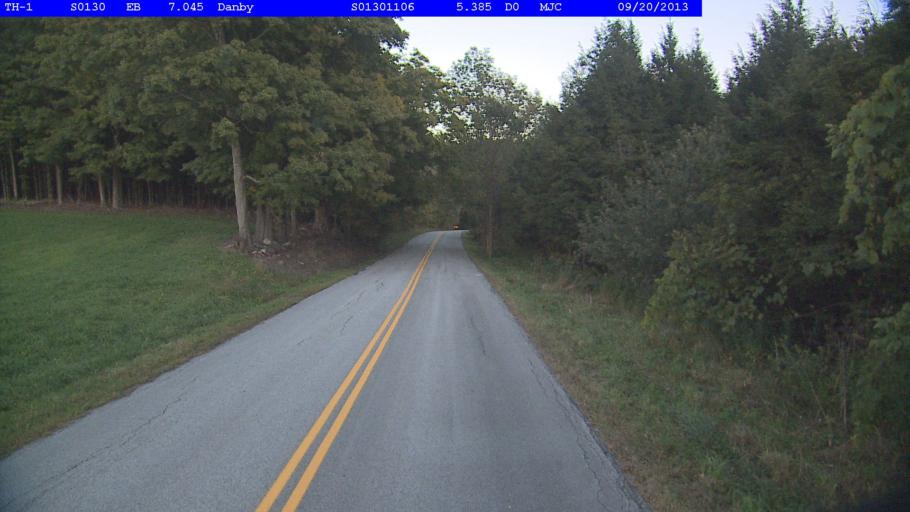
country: US
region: Vermont
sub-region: Bennington County
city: Manchester Center
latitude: 43.3398
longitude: -73.0417
